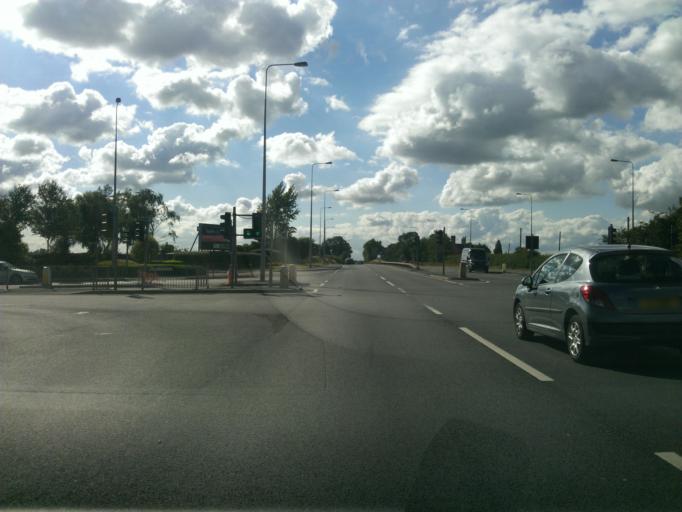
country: GB
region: England
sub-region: Warwickshire
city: Kingsbury
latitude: 52.6006
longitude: -1.6261
